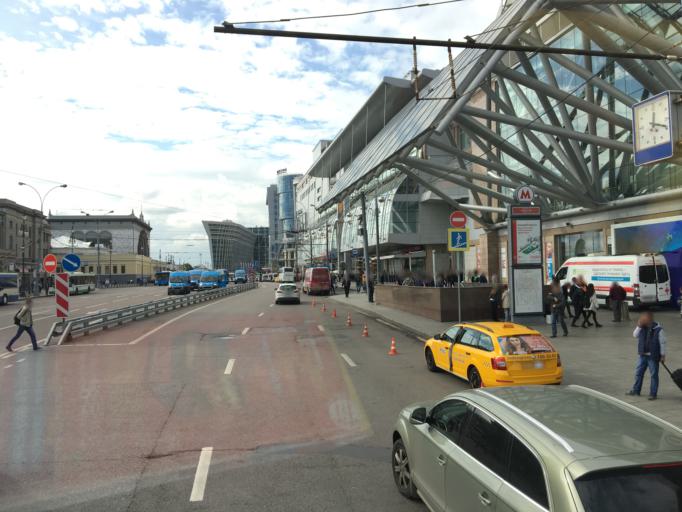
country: RU
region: Moskovskaya
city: Dorogomilovo
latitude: 55.7441
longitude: 37.5675
